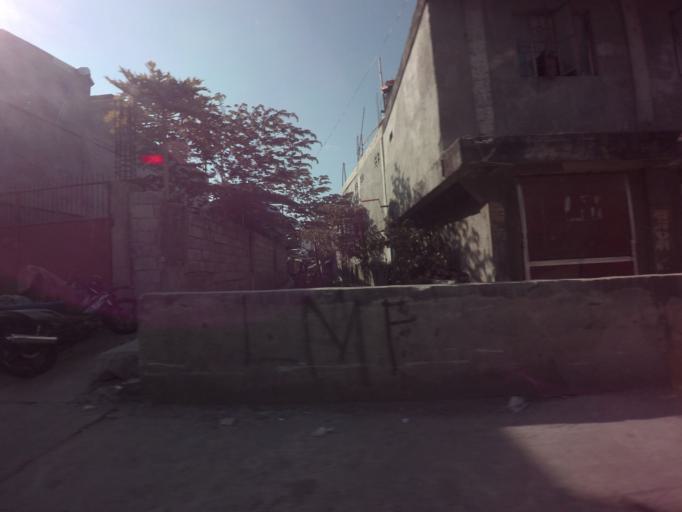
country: PH
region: Calabarzon
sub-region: Province of Rizal
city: Taguig
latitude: 14.4990
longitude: 121.0576
